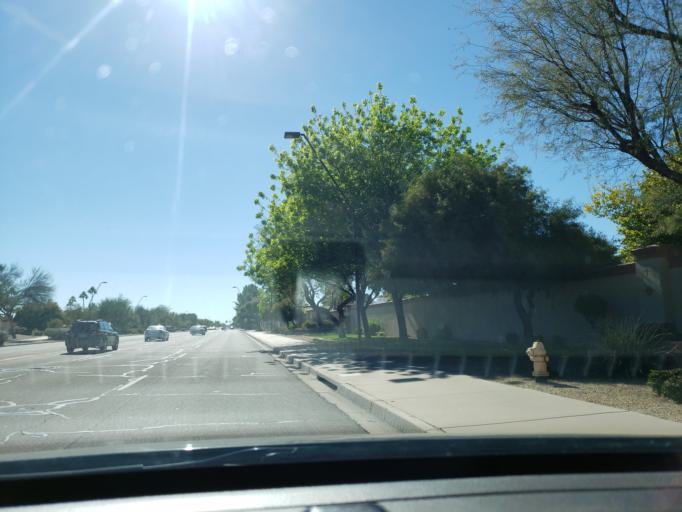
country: US
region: Arizona
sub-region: Maricopa County
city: Guadalupe
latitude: 33.3458
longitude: -111.9286
